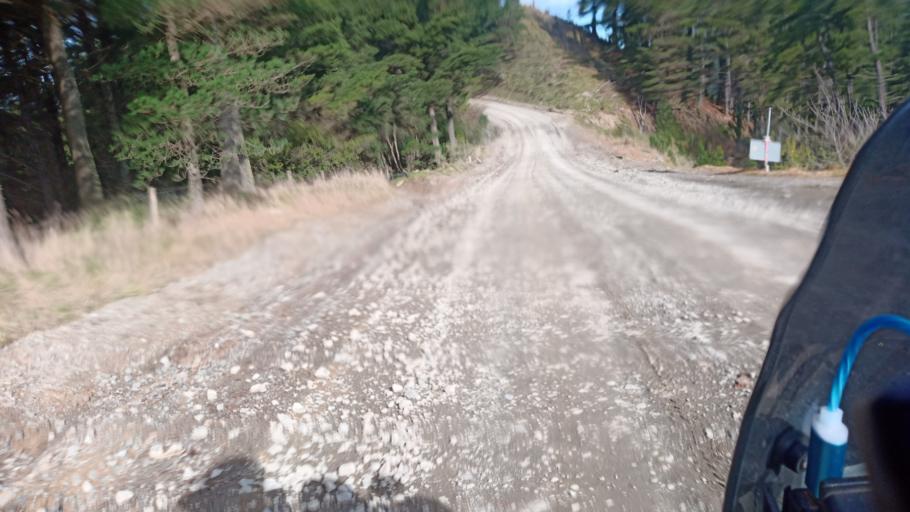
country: NZ
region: Gisborne
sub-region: Gisborne District
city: Gisborne
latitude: -38.1228
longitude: 178.1581
